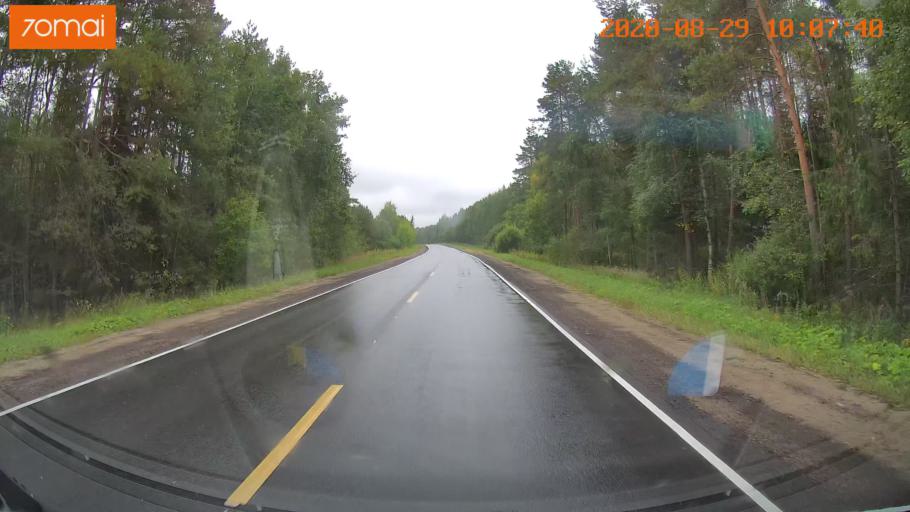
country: RU
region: Ivanovo
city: Kuznechikha
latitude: 57.3792
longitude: 42.5717
